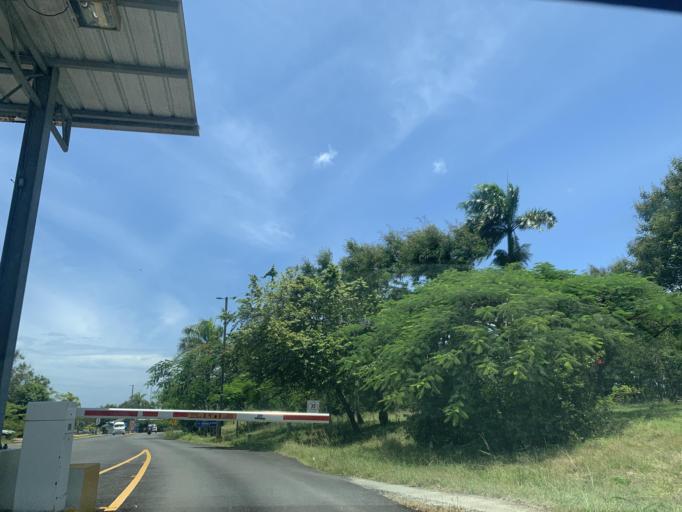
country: DO
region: Puerto Plata
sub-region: Puerto Plata
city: Puerto Plata
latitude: 19.7538
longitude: -70.5614
